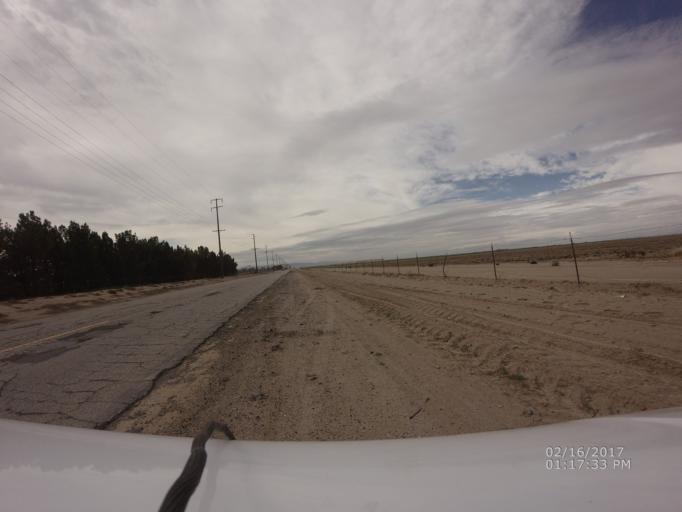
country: US
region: California
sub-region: Los Angeles County
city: Palmdale
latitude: 34.6314
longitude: -118.0293
